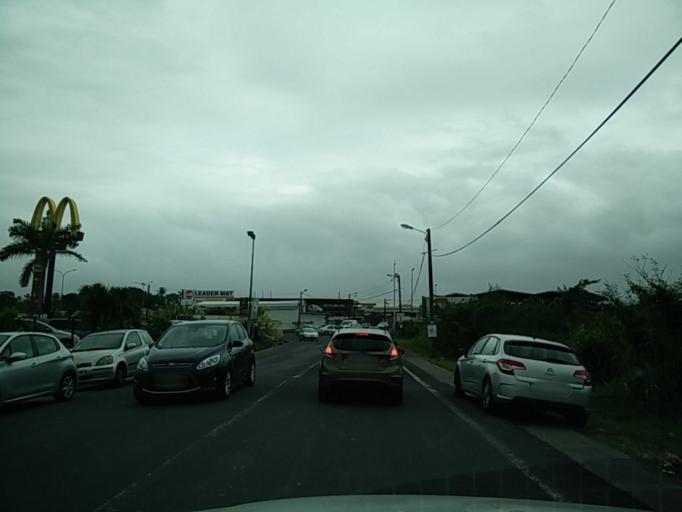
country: GP
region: Guadeloupe
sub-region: Guadeloupe
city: Baie-Mahault
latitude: 16.2536
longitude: -61.5618
